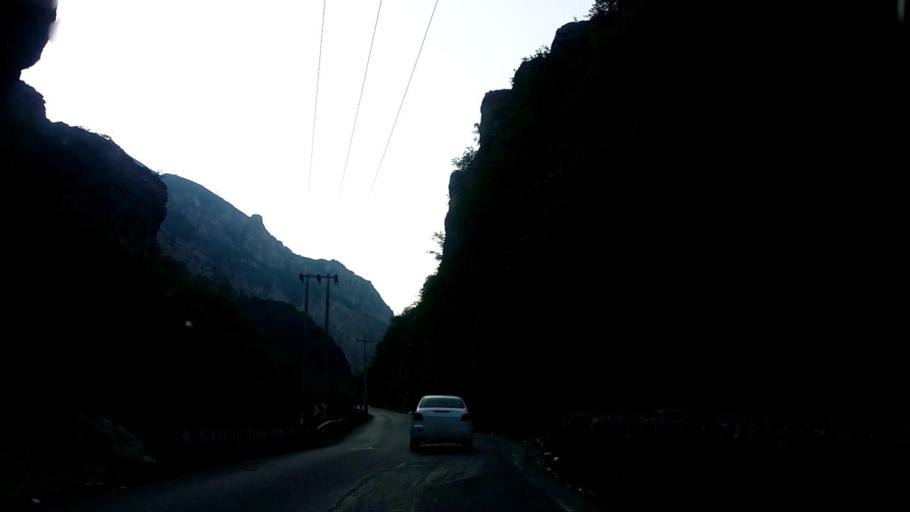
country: IR
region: Mazandaran
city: Chalus
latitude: 36.2701
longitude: 51.2521
